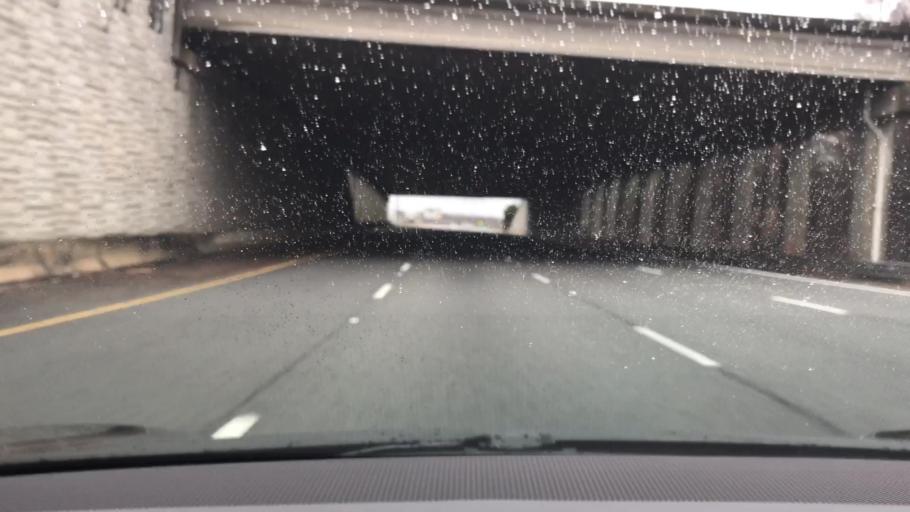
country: US
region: Georgia
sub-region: Gwinnett County
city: Duluth
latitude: 33.9828
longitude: -84.0875
